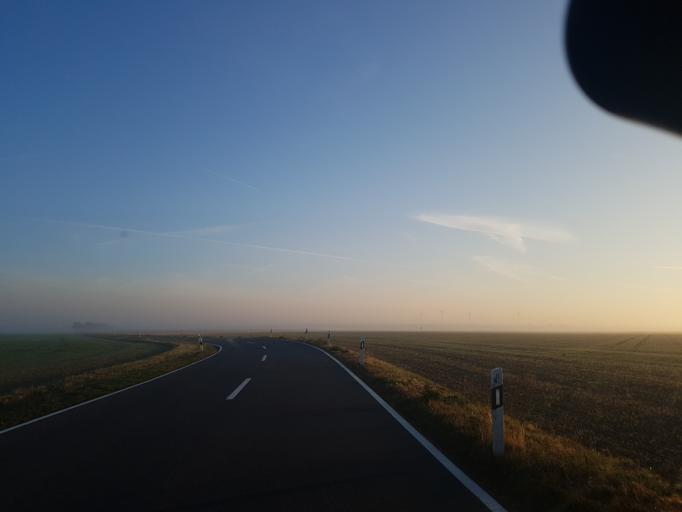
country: DE
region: Brandenburg
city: Juterbog
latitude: 51.8977
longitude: 13.0711
